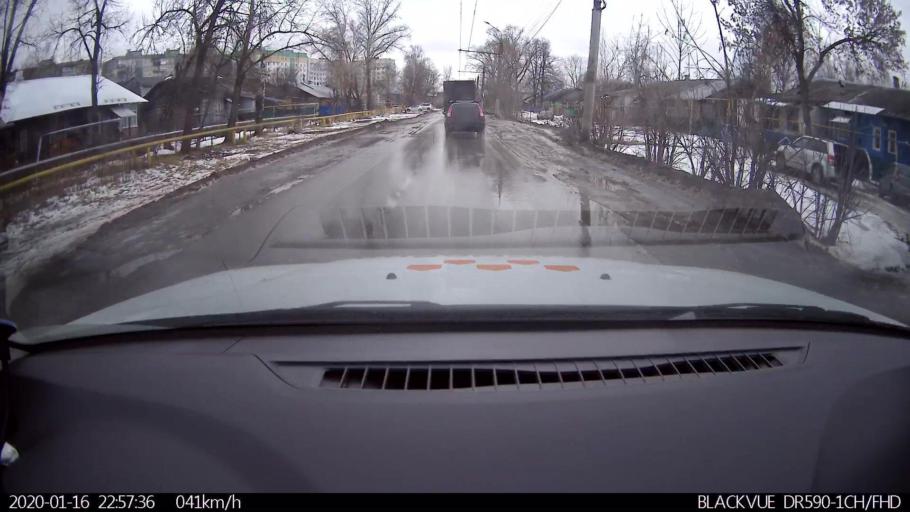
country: RU
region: Nizjnij Novgorod
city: Nizhniy Novgorod
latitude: 56.2916
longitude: 43.9087
